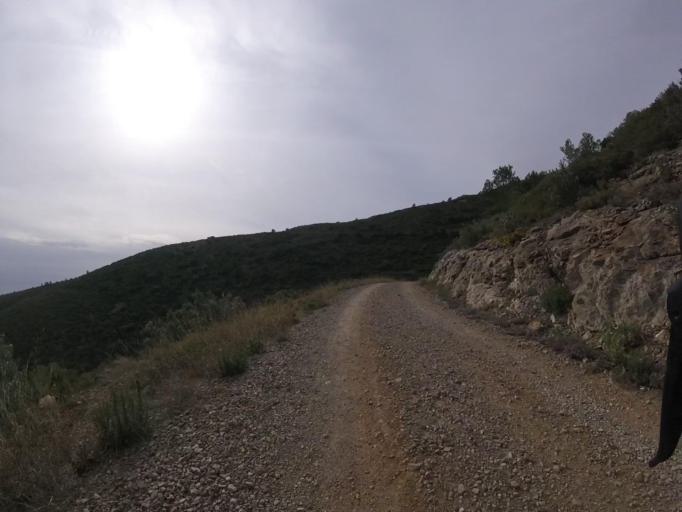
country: ES
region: Valencia
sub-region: Provincia de Castello
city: Benicassim
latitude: 40.0985
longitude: 0.0460
